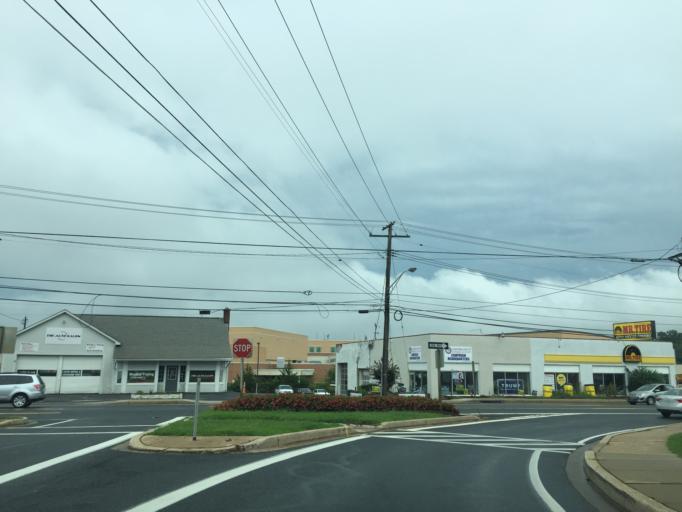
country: US
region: Maryland
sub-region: Harford County
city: Bel Air
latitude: 39.5324
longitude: -76.3491
